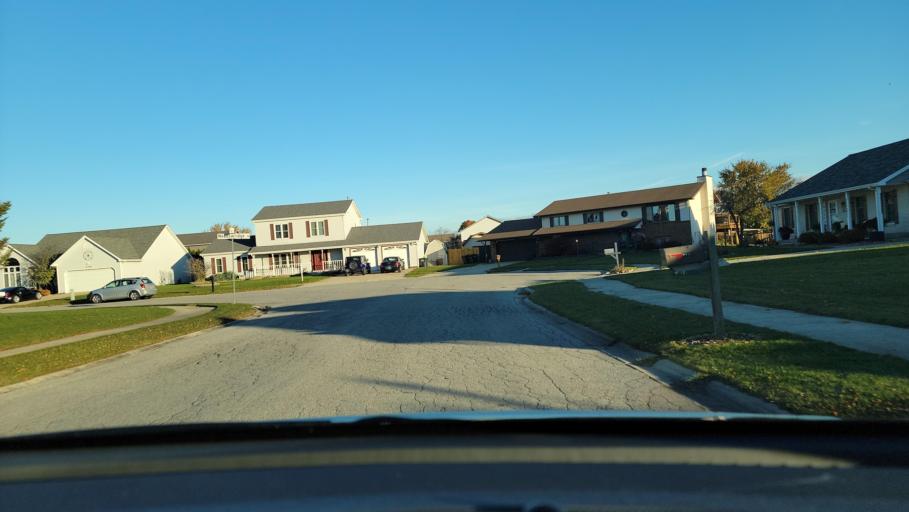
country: US
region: Indiana
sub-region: Porter County
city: Portage
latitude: 41.5615
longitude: -87.1645
